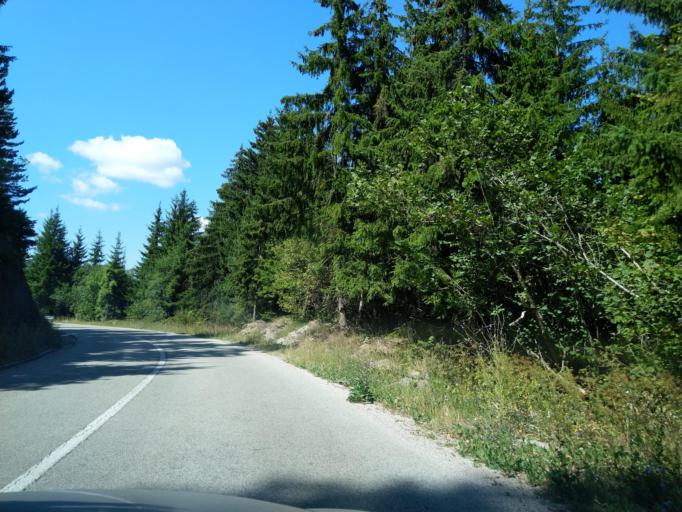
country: RS
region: Central Serbia
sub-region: Zlatiborski Okrug
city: Nova Varos
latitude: 43.3529
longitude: 19.8538
